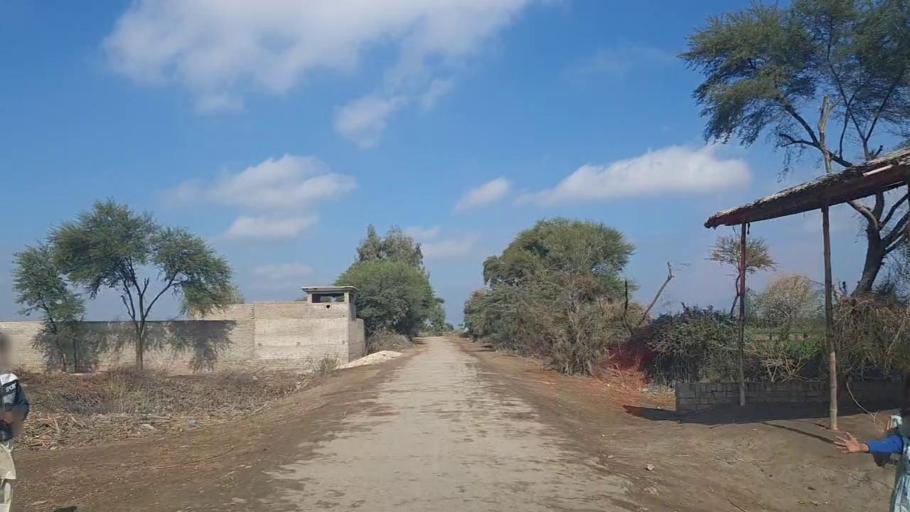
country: PK
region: Sindh
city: Sanghar
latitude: 26.0639
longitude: 68.9907
